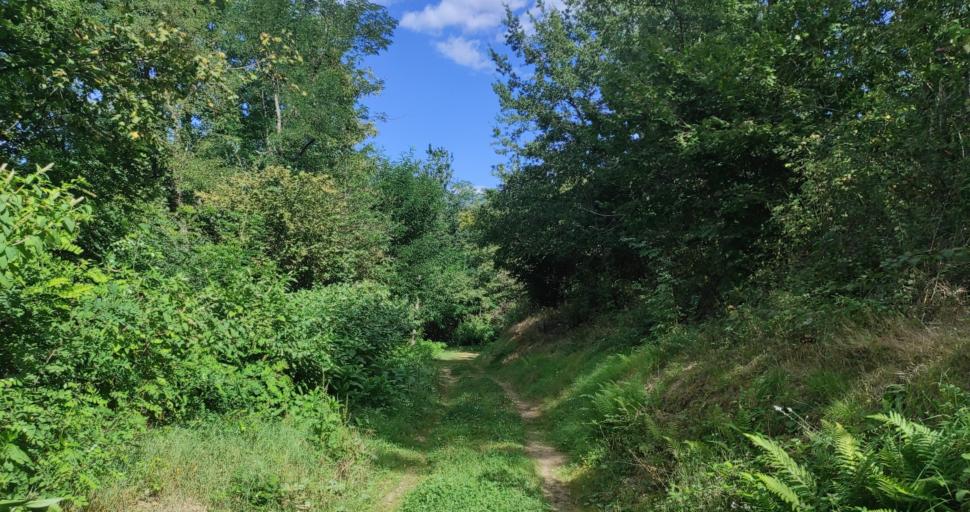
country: FR
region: Midi-Pyrenees
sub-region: Departement de l'Aveyron
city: Cransac
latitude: 44.5311
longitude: 2.2731
